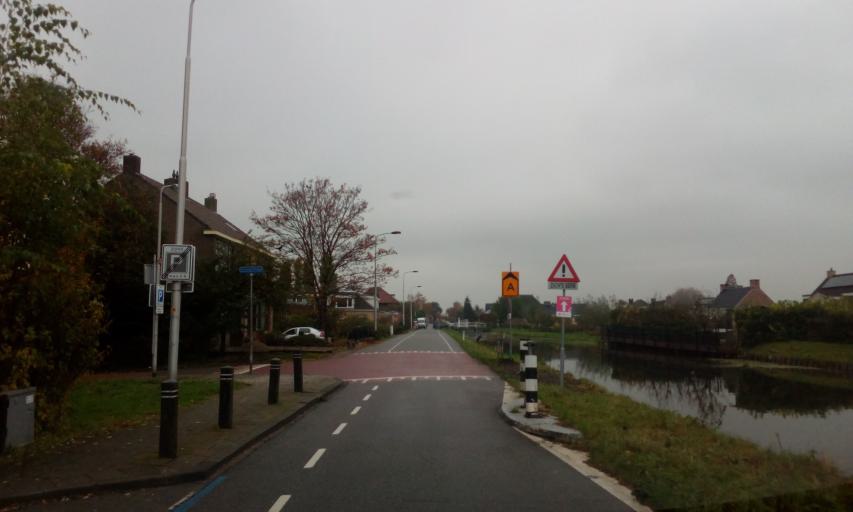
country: NL
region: South Holland
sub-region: Gemeente Lansingerland
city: Berkel en Rodenrijs
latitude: 51.9751
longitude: 4.4558
